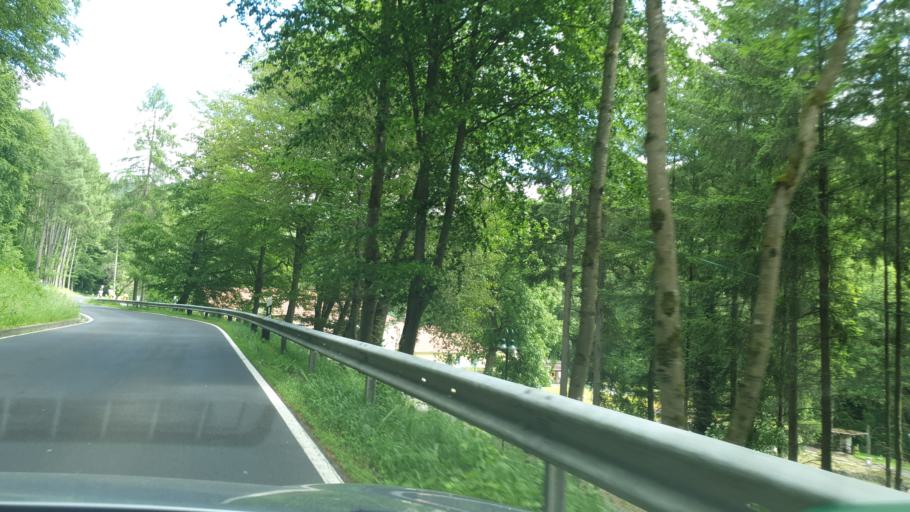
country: DE
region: Rheinland-Pfalz
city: Hillscheid
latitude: 50.3974
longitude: 7.7139
